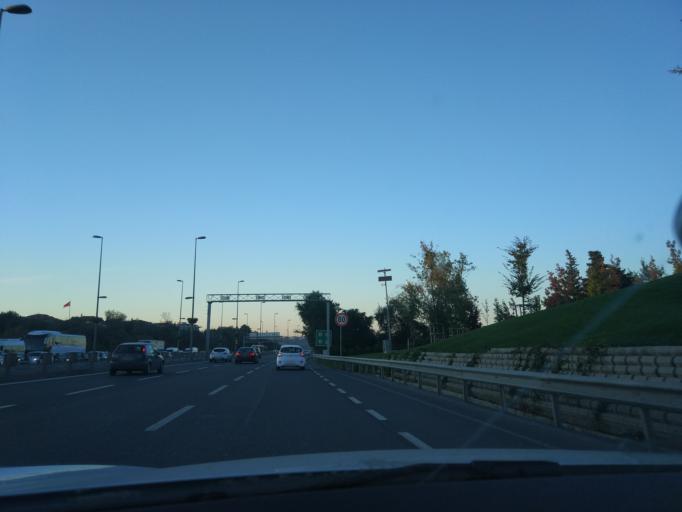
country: TR
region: Istanbul
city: UEskuedar
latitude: 41.0271
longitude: 29.0462
